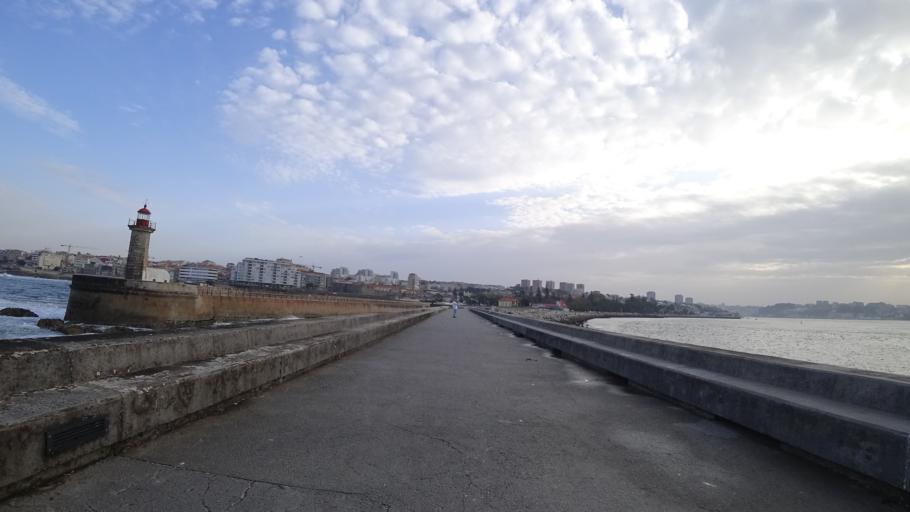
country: PT
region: Porto
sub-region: Vila Nova de Gaia
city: Canidelo
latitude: 41.1462
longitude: -8.6774
